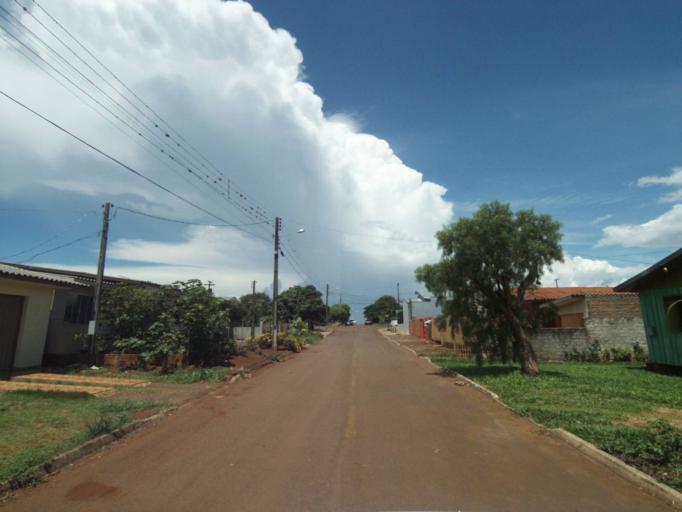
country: BR
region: Parana
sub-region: Guaraniacu
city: Guaraniacu
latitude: -25.0932
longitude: -52.8748
